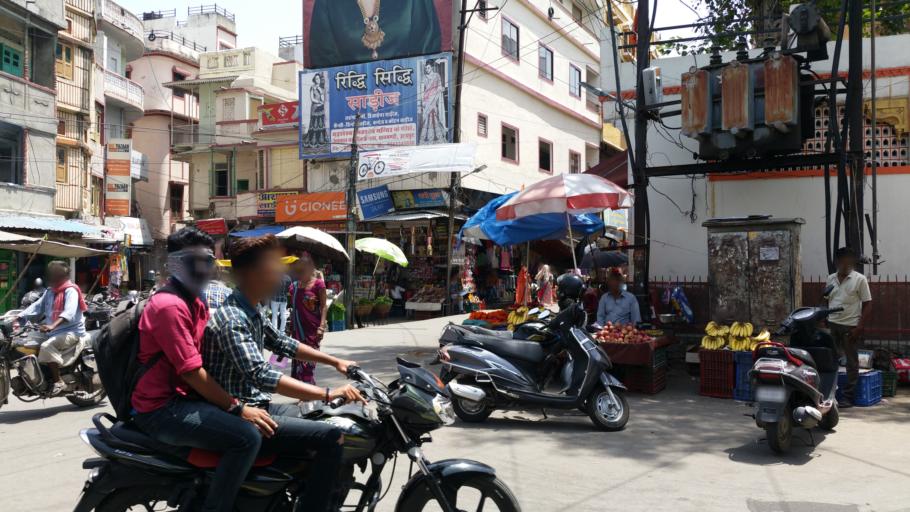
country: IN
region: Rajasthan
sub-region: Udaipur
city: Udaipur
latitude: 24.5841
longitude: 73.6945
